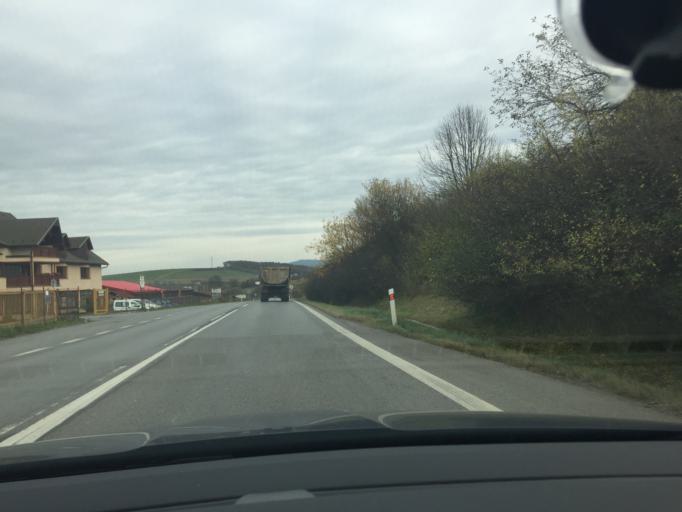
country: SK
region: Presovsky
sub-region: Okres Presov
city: Presov
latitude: 49.0050
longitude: 21.1712
